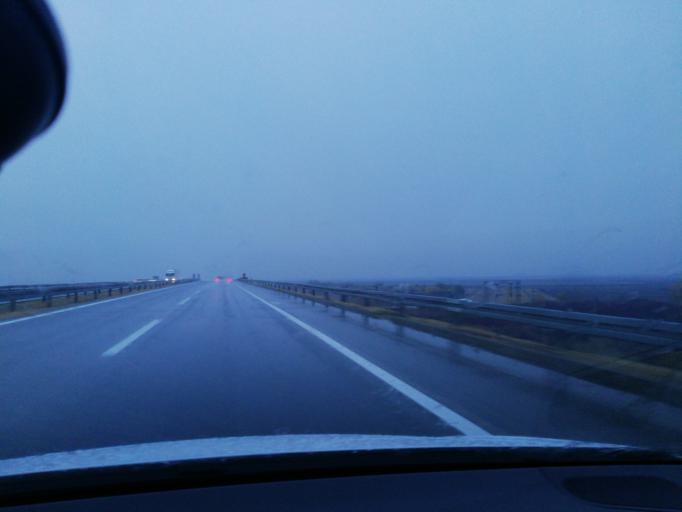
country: RS
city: Sasinci
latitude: 44.9875
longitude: 19.7126
